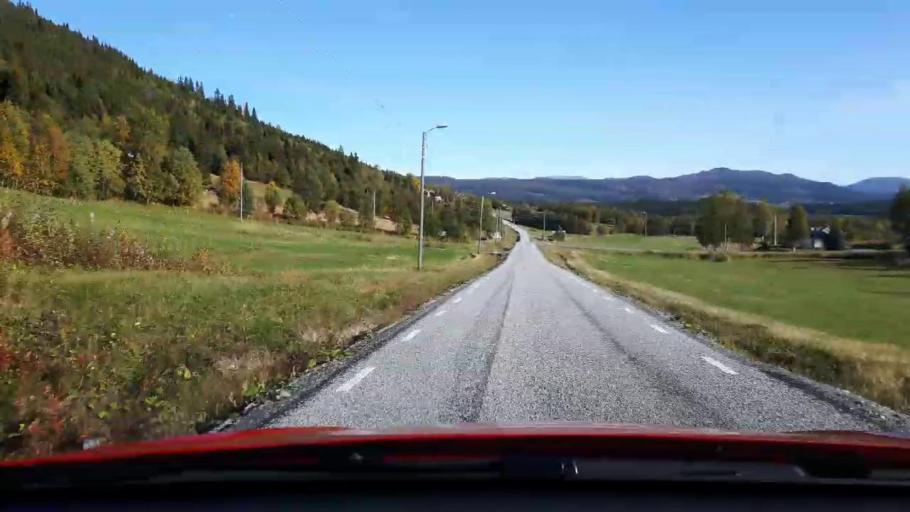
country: NO
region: Nord-Trondelag
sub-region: Royrvik
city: Royrvik
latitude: 64.7290
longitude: 13.9477
